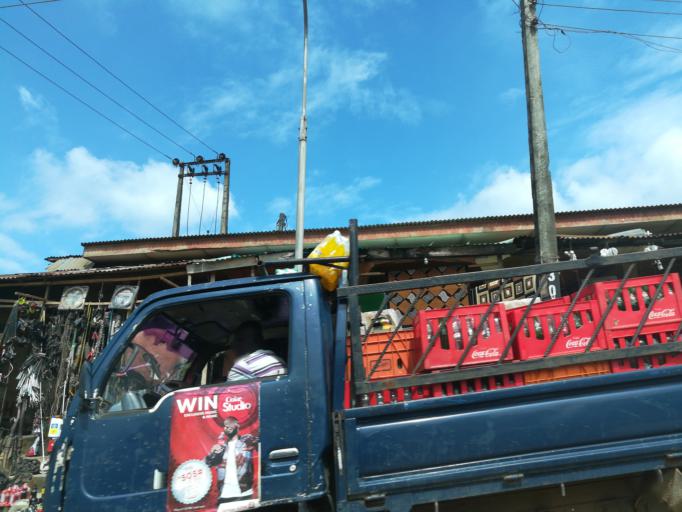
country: NG
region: Lagos
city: Ikorodu
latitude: 6.6001
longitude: 3.5184
